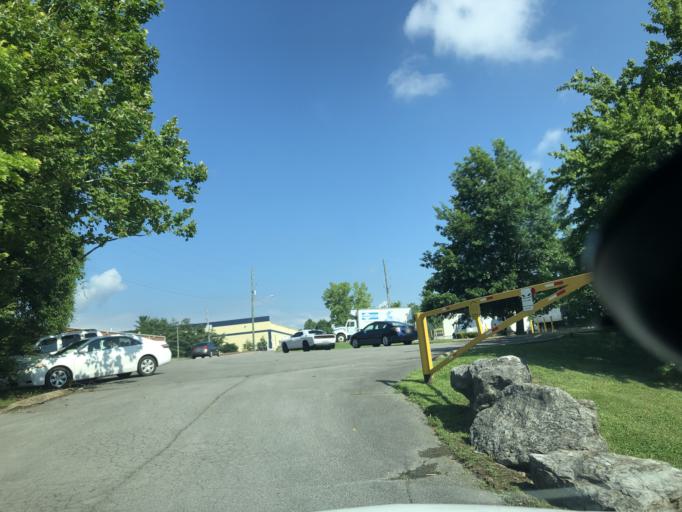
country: US
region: Tennessee
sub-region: Rutherford County
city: La Vergne
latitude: 36.0111
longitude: -86.6141
